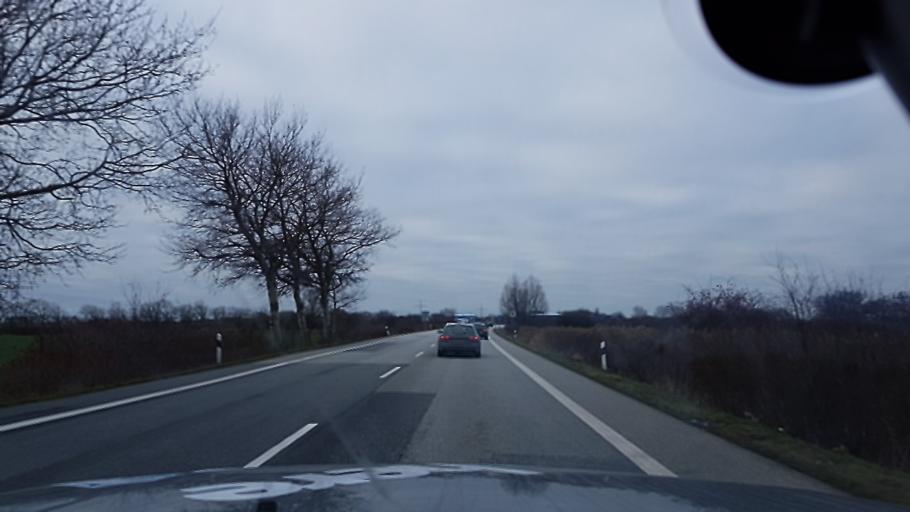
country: DE
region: Schleswig-Holstein
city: Grossenbrode
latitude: 54.3849
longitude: 11.0983
